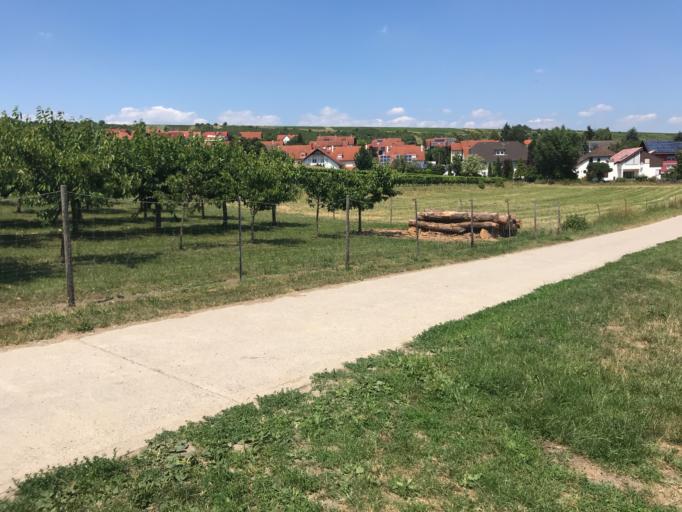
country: DE
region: Rheinland-Pfalz
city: Jugenheim
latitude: 49.8899
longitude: 8.0813
